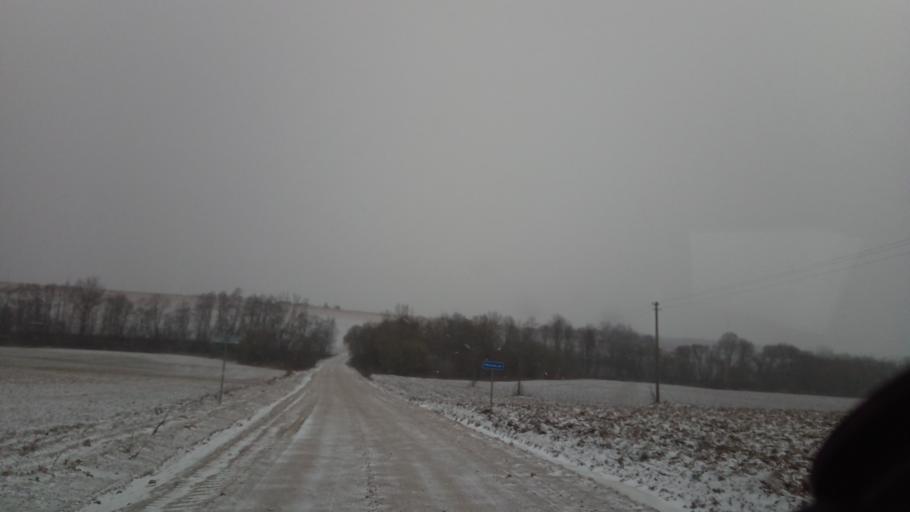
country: LT
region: Vilnius County
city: Ukmerge
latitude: 55.3404
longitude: 24.9588
